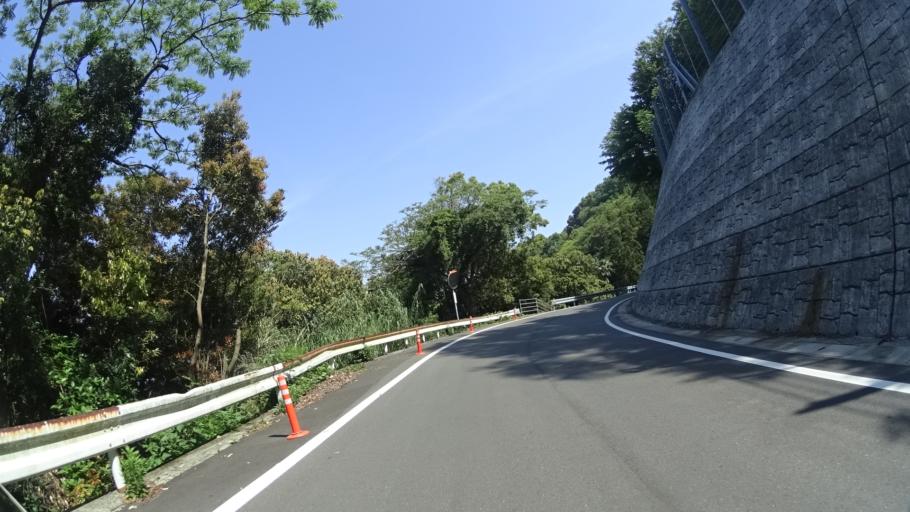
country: JP
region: Oita
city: Tsukumiura
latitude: 33.3541
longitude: 132.0319
